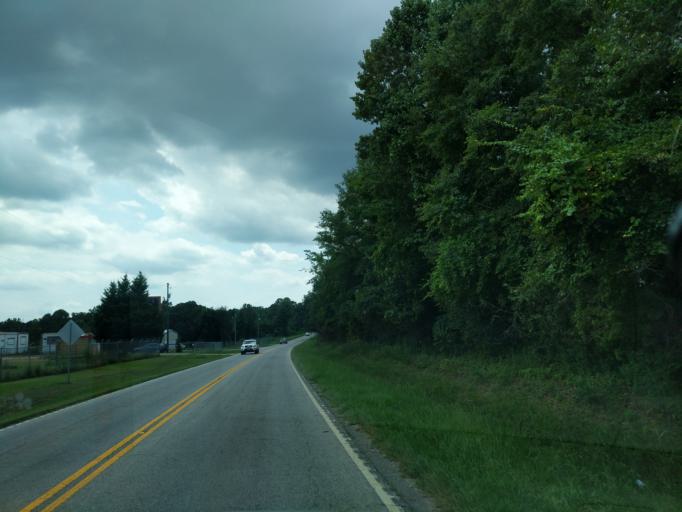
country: US
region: South Carolina
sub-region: Spartanburg County
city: Wellford
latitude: 34.9885
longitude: -82.1107
